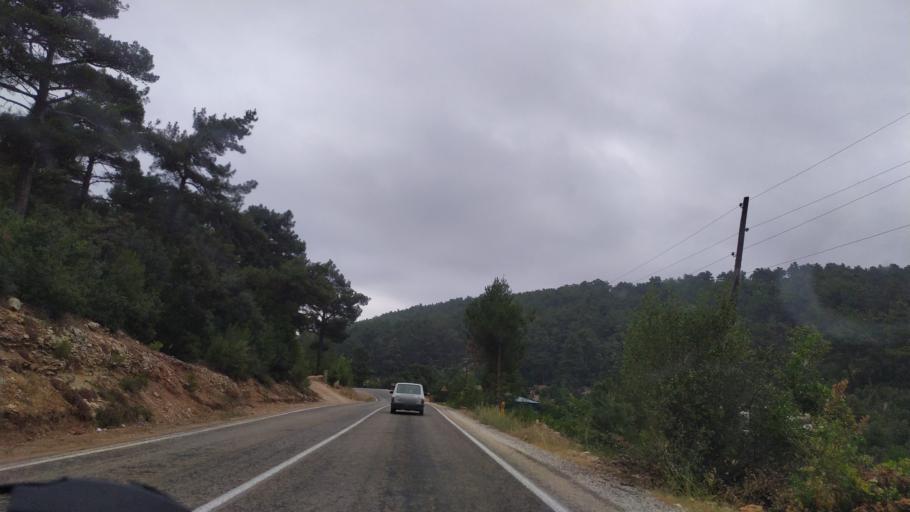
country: TR
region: Mersin
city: Silifke
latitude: 36.5391
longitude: 33.9410
